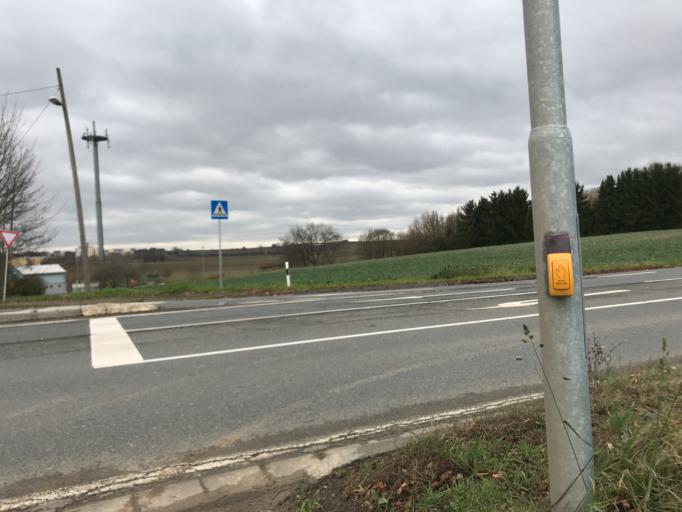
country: DE
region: Rheinland-Pfalz
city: Gau-Bischofsheim
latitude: 49.9197
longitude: 8.2675
